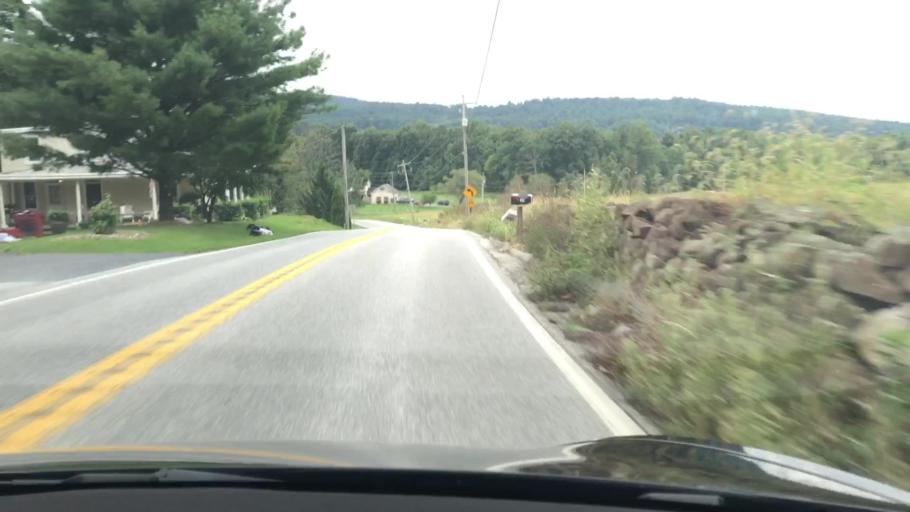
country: US
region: Pennsylvania
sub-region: York County
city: Dillsburg
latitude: 40.1311
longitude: -76.9615
